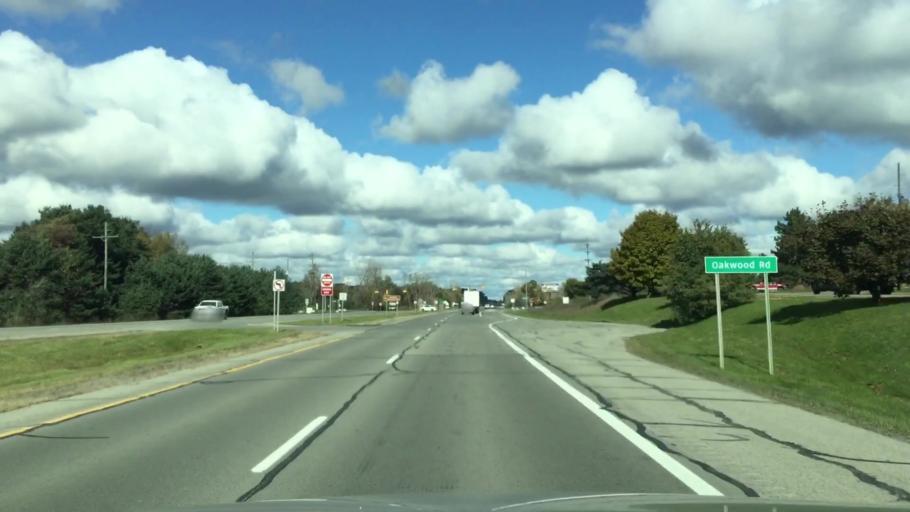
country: US
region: Michigan
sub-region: Oakland County
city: Oxford
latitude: 42.8671
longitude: -83.2941
